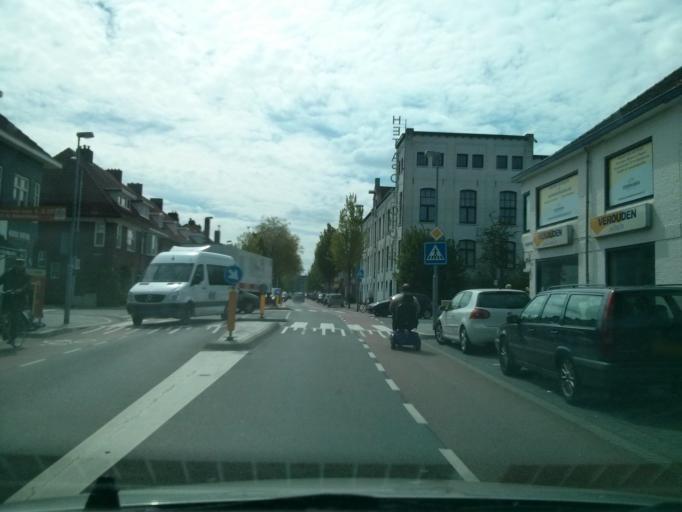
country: NL
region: North Brabant
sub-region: Gemeente Eindhoven
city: Villapark
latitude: 51.4398
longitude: 5.4957
